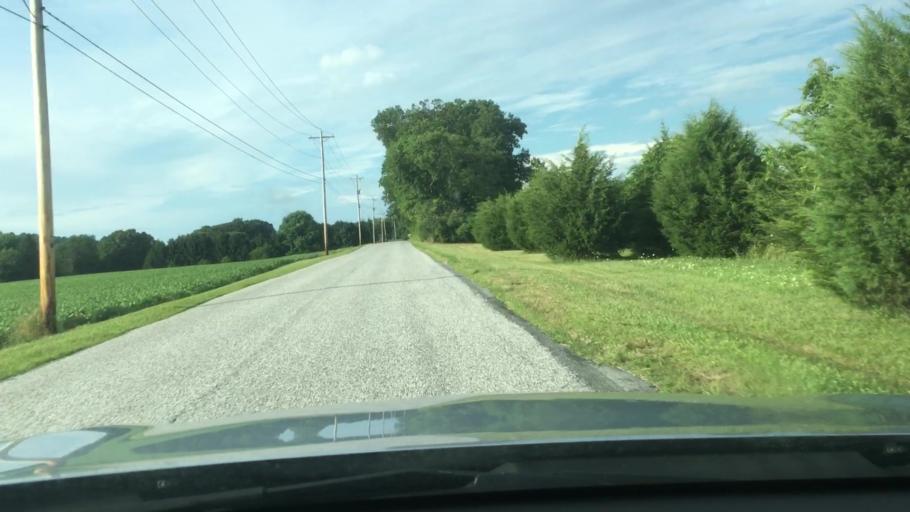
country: US
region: Pennsylvania
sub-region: York County
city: Dover
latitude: 40.0245
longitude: -76.8478
